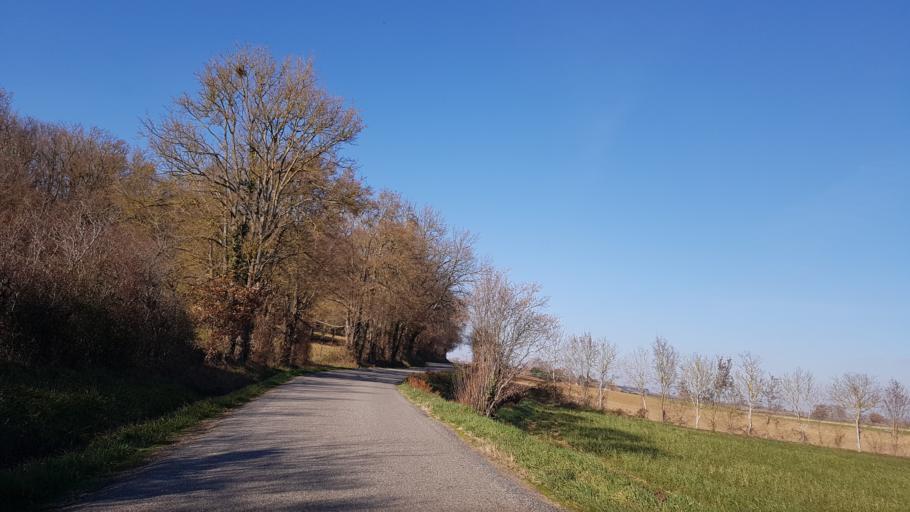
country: FR
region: Midi-Pyrenees
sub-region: Departement de l'Ariege
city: La Tour-du-Crieu
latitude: 43.1246
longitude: 1.7207
